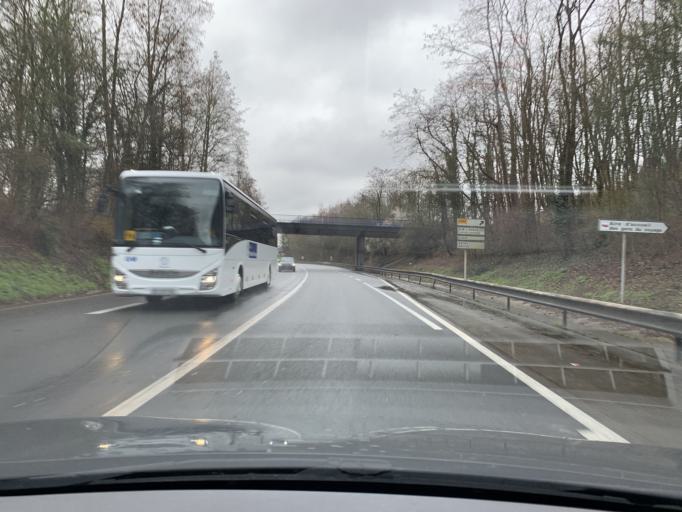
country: FR
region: Nord-Pas-de-Calais
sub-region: Departement du Nord
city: Dechy
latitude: 50.3514
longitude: 3.1209
